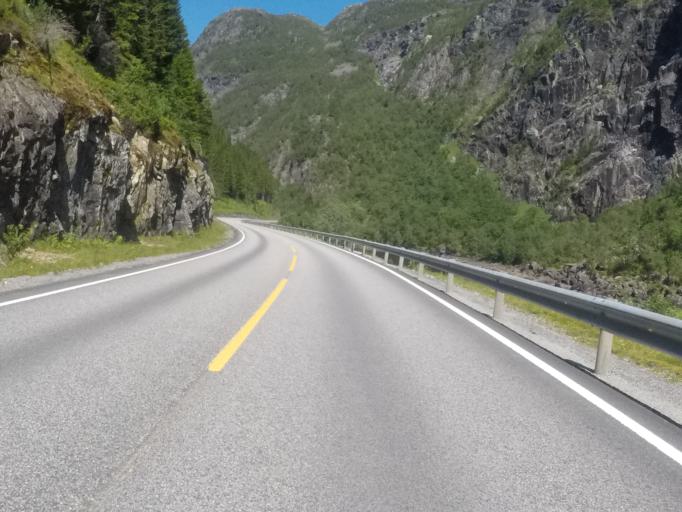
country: NO
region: Sogn og Fjordane
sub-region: Eid
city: Nordfjordeid
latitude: 61.9661
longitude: 6.1321
